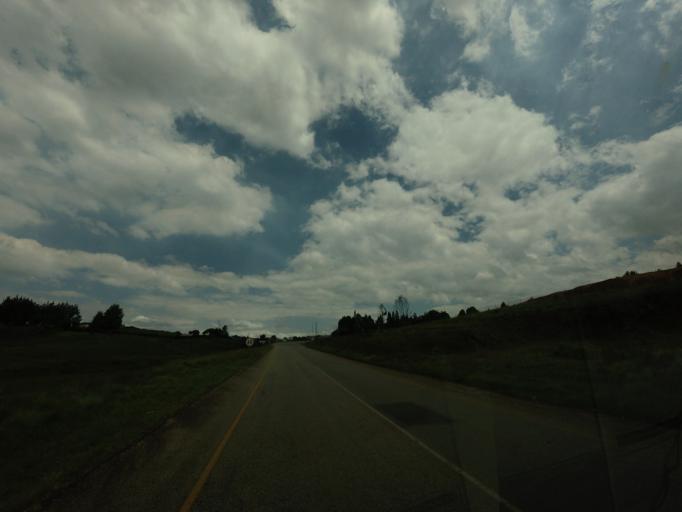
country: ZA
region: Mpumalanga
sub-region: Ehlanzeni District
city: Graksop
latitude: -24.9257
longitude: 30.8363
